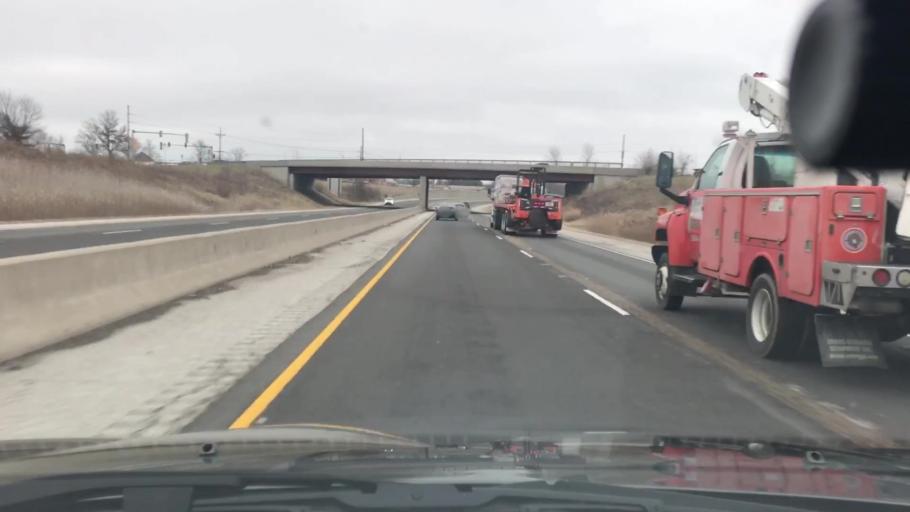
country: US
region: Illinois
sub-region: Madison County
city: Rosewood Heights
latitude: 38.8888
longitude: -90.0608
